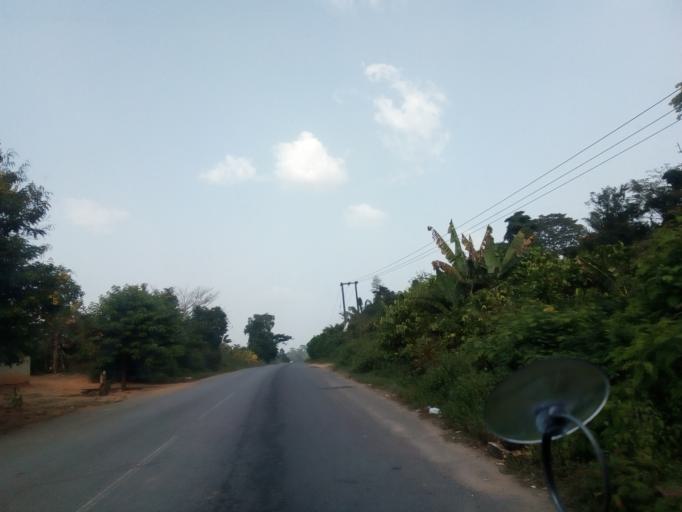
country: GH
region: Eastern
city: Suhum
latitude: 6.0478
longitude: -0.4109
